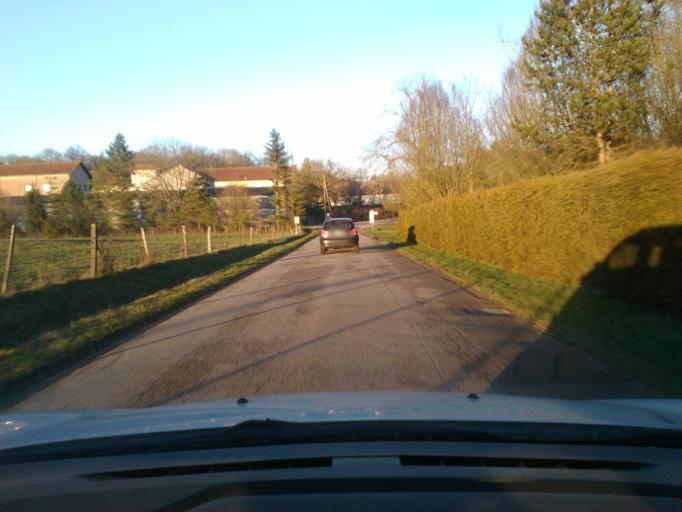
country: FR
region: Lorraine
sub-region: Departement des Vosges
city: Mirecourt
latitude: 48.2928
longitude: 6.1189
